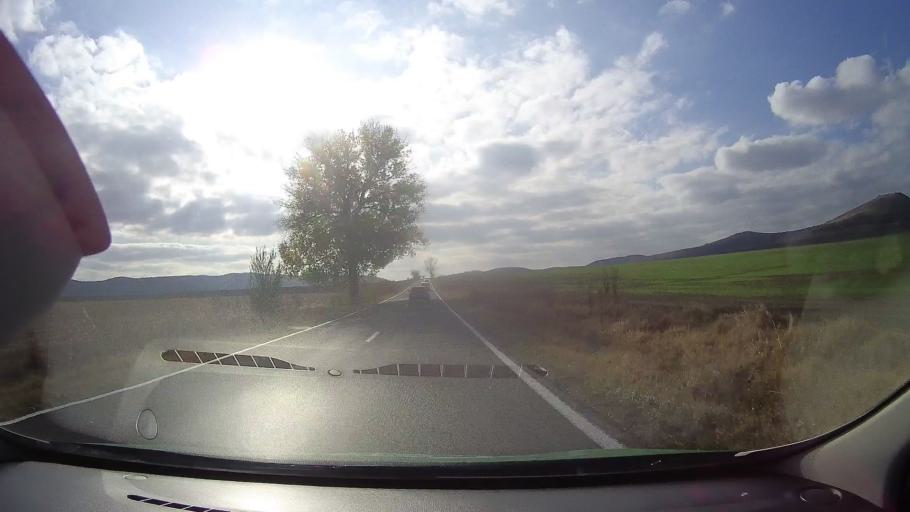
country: RO
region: Tulcea
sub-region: Comuna Nalbant
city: Nicolae Balcescu
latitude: 44.9880
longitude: 28.5582
